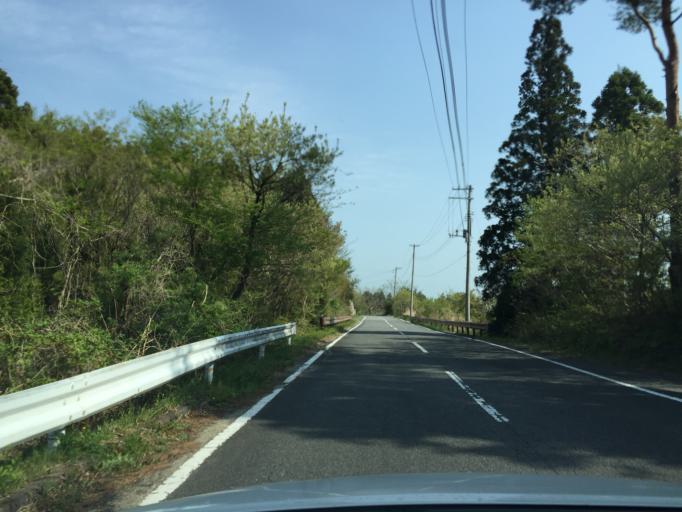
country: JP
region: Fukushima
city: Iwaki
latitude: 37.1586
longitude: 140.8541
